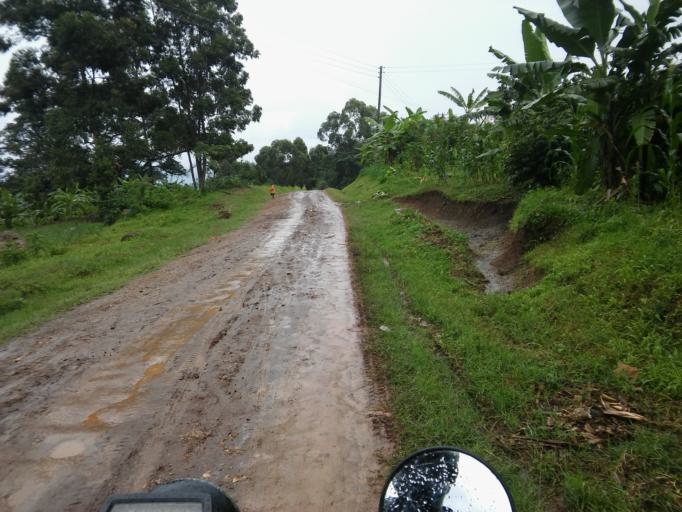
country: UG
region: Eastern Region
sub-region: Bududa District
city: Bududa
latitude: 1.0067
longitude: 34.2383
